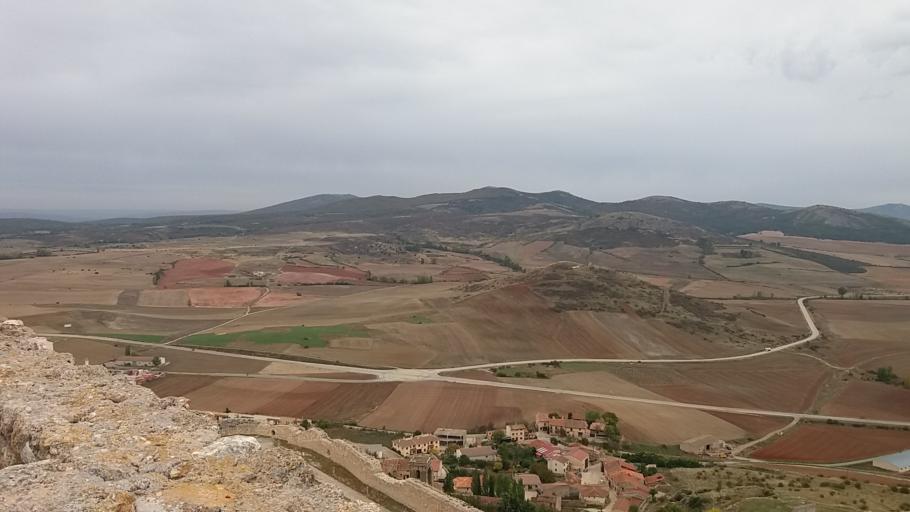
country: ES
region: Castille-La Mancha
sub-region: Provincia de Guadalajara
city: Atienza
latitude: 41.1996
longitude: -2.8741
